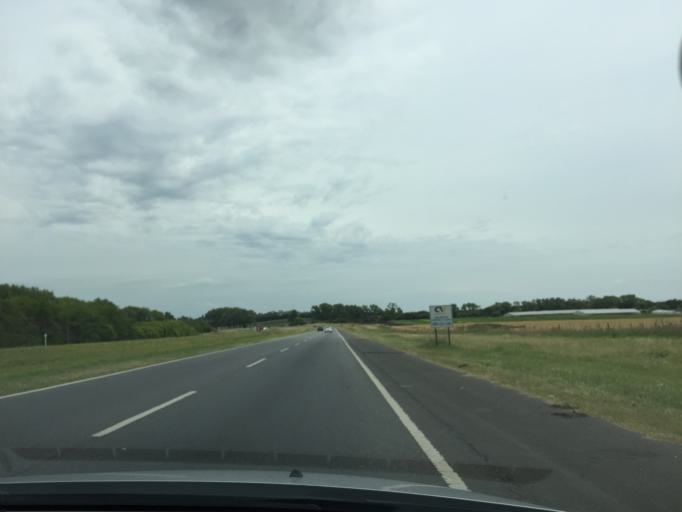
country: AR
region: Buenos Aires
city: Mar del Plata
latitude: -37.9357
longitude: -57.6659
